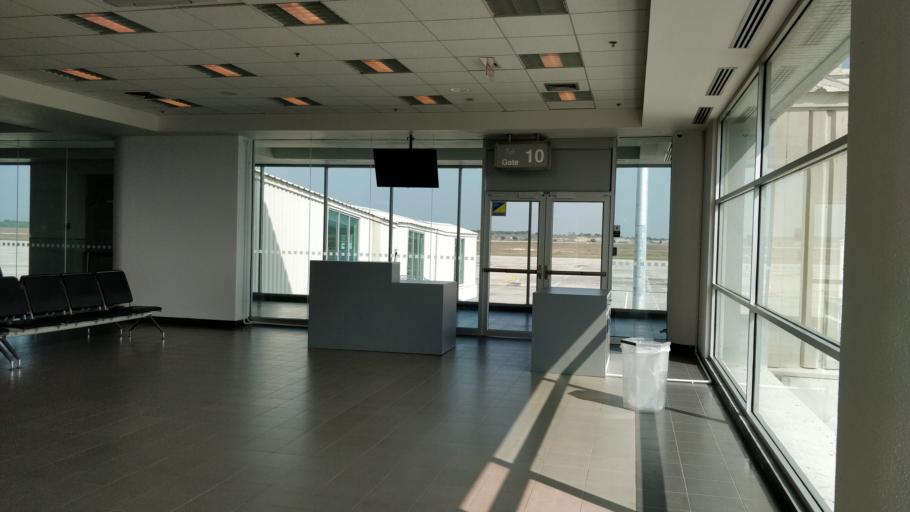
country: MM
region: Sagain
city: Sagaing
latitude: 21.7047
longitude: 95.9708
